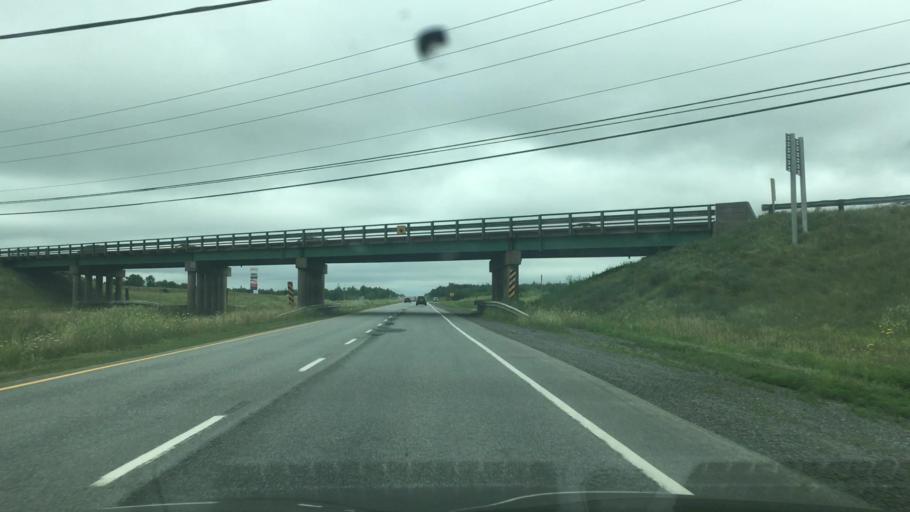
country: CA
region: Nova Scotia
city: Cole Harbour
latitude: 44.9774
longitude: -63.5078
